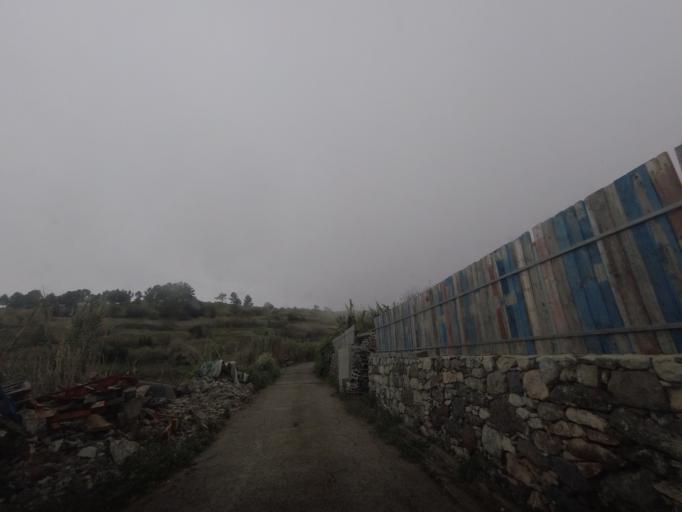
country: PT
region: Madeira
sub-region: Calheta
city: Faja da Ovelha
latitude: 32.7591
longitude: -17.2197
